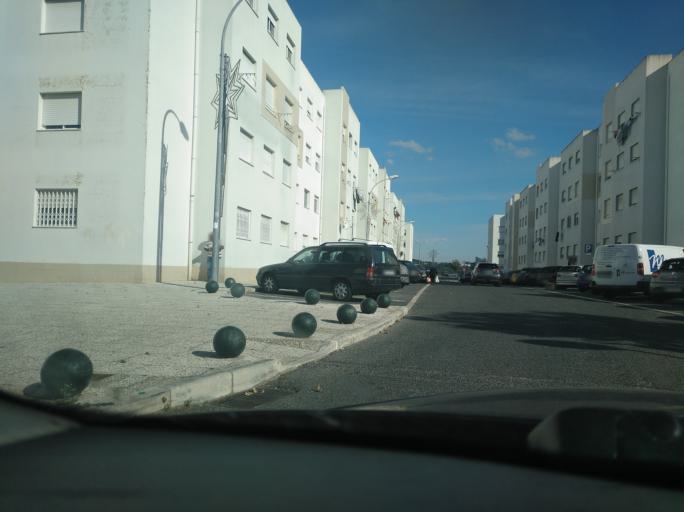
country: PT
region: Lisbon
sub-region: Oeiras
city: Linda-a-Velha
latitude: 38.7181
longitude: -9.2317
